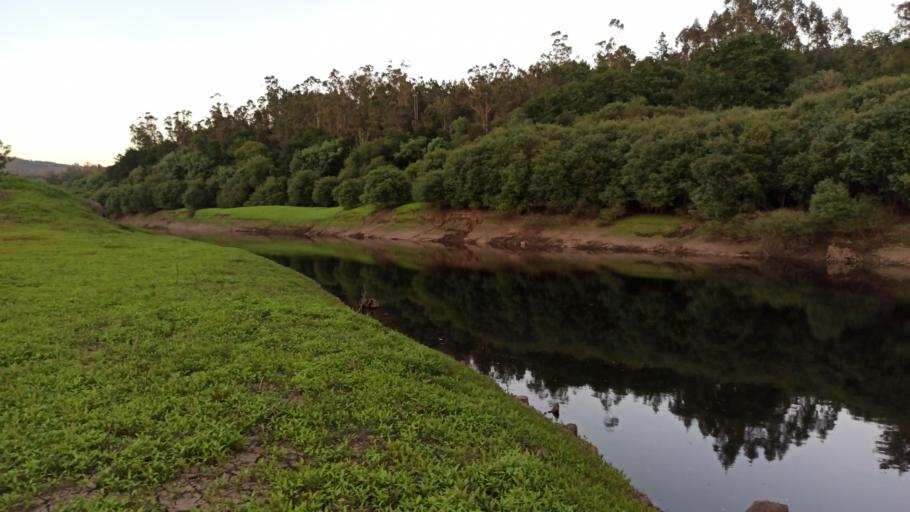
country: ES
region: Galicia
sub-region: Provincia da Coruna
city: Negreira
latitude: 42.8980
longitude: -8.7372
